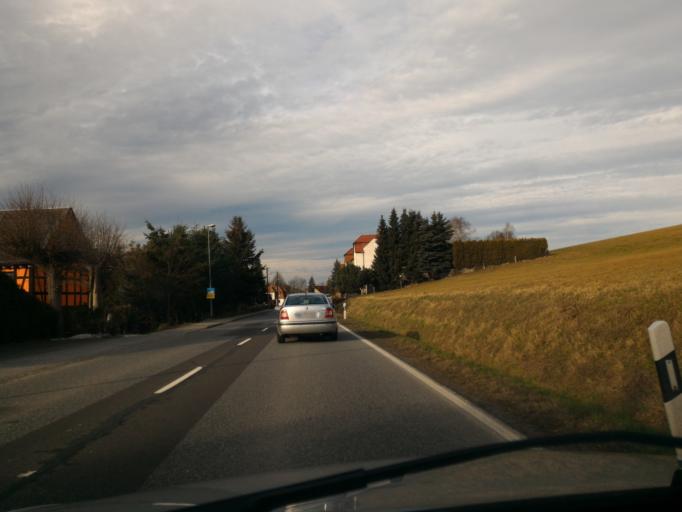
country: DE
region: Saxony
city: Demitz-Thumitz
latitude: 51.1019
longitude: 14.2279
